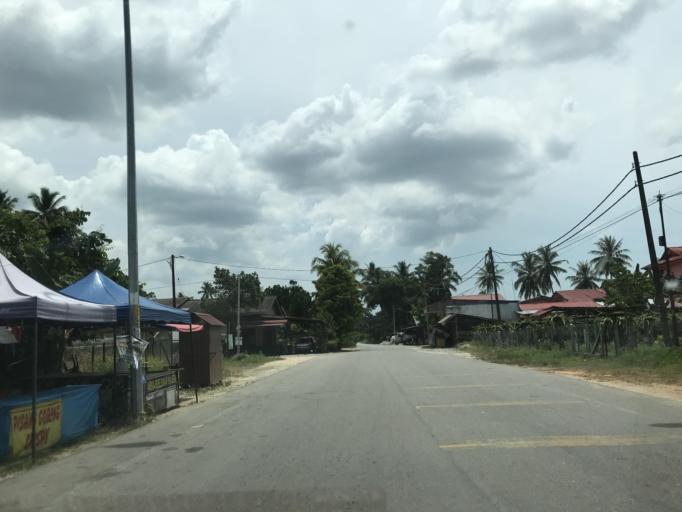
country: MY
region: Kelantan
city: Kota Bharu
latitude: 6.1460
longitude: 102.1871
